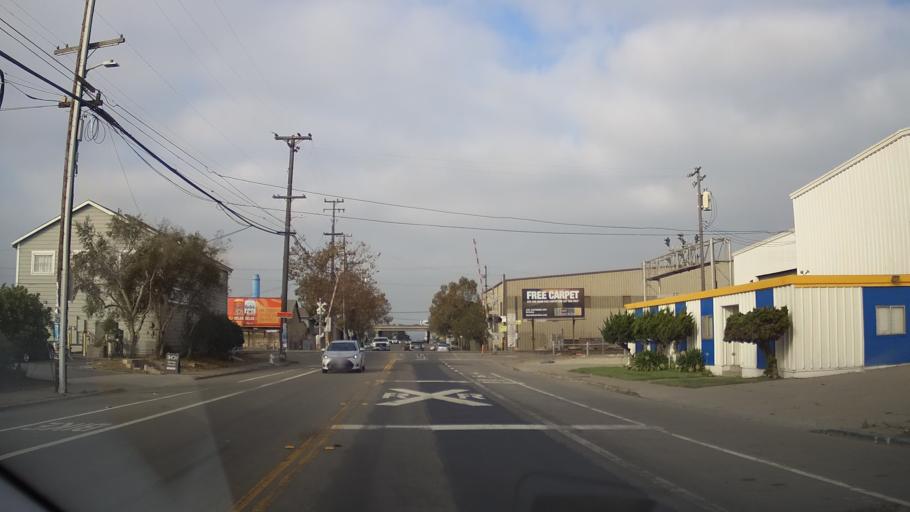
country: US
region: California
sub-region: Alameda County
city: Albany
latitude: 37.8789
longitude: -122.3038
